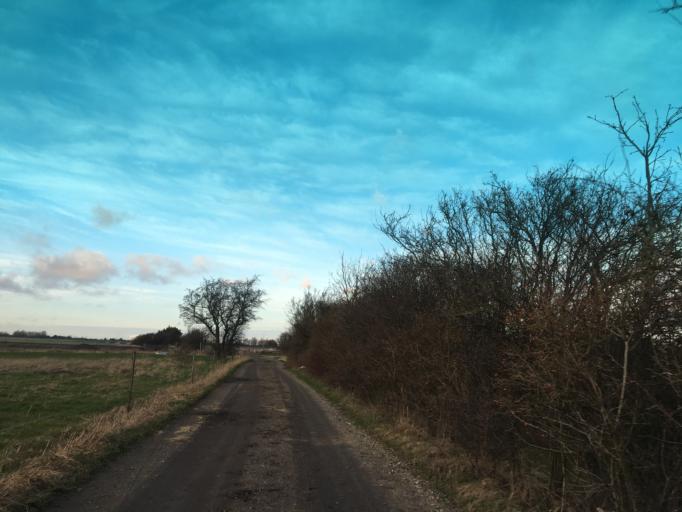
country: DK
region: Capital Region
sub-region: Tarnby Kommune
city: Tarnby
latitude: 55.5953
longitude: 12.6217
